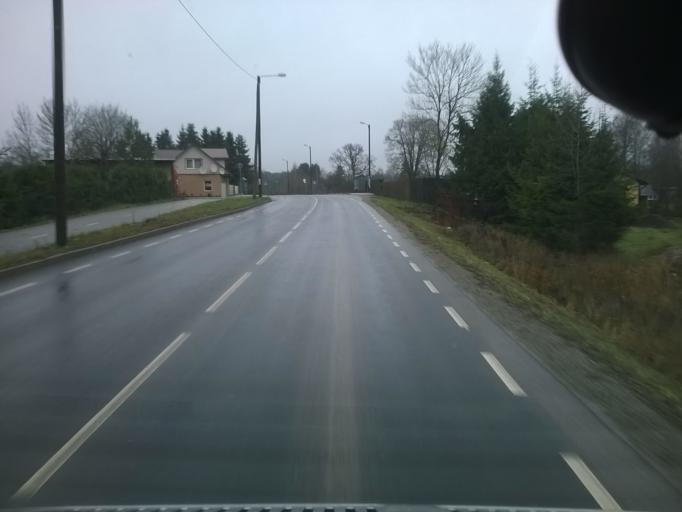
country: EE
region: Harju
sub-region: Saku vald
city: Saku
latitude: 59.2159
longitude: 24.6637
